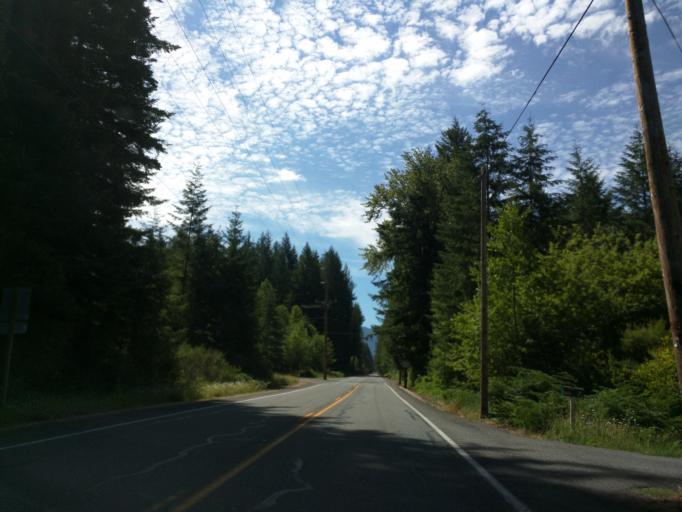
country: US
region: Washington
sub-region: Whatcom County
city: Peaceful Valley
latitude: 48.9581
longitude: -122.1580
